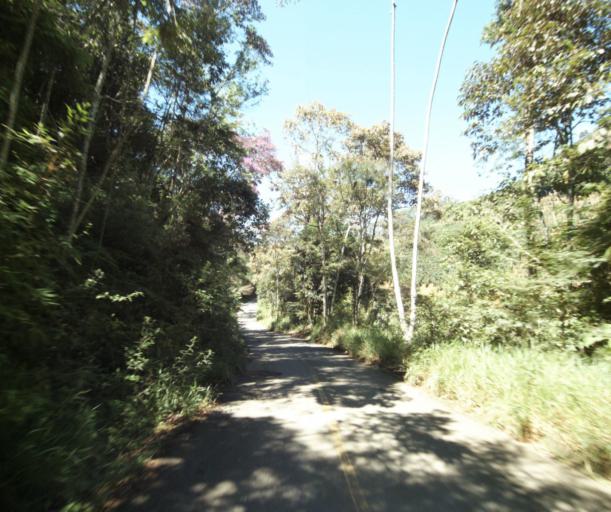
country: BR
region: Minas Gerais
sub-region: Espera Feliz
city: Espera Feliz
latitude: -20.6375
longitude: -41.8189
